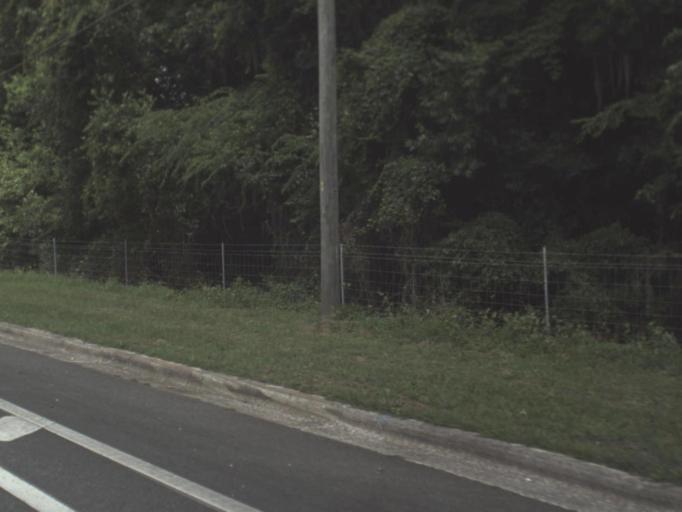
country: US
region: Florida
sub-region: Alachua County
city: Gainesville
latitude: 29.6242
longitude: -82.3255
